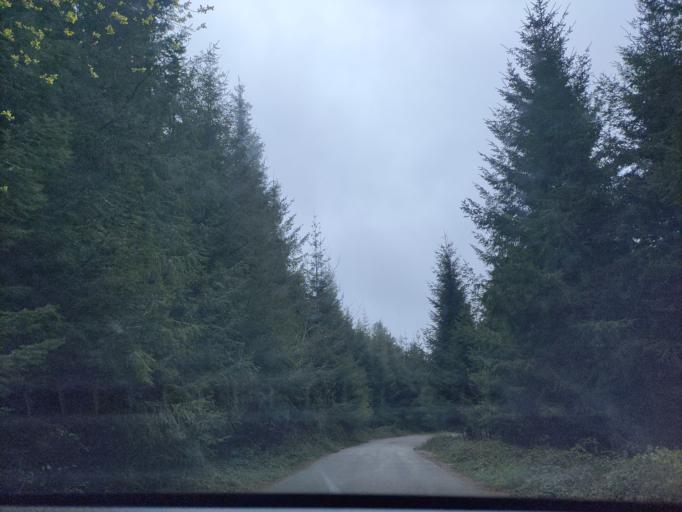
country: ES
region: Catalonia
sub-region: Provincia de Barcelona
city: Fogars de Montclus
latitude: 41.7582
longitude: 2.4579
